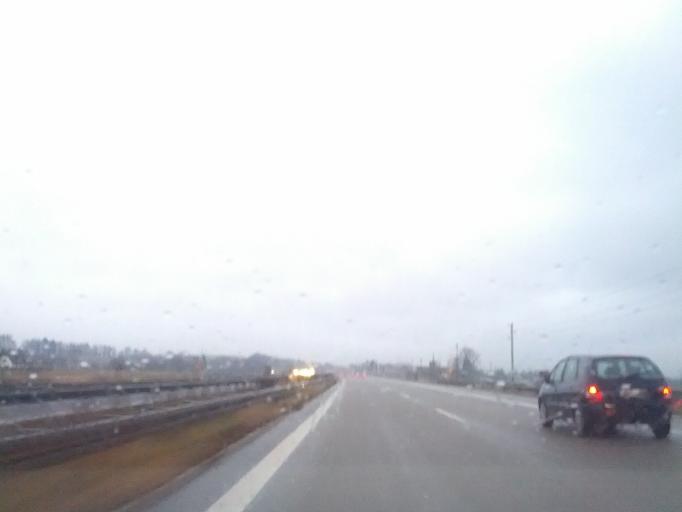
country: DE
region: Bavaria
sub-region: Swabia
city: Benningen
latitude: 47.9522
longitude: 10.1936
